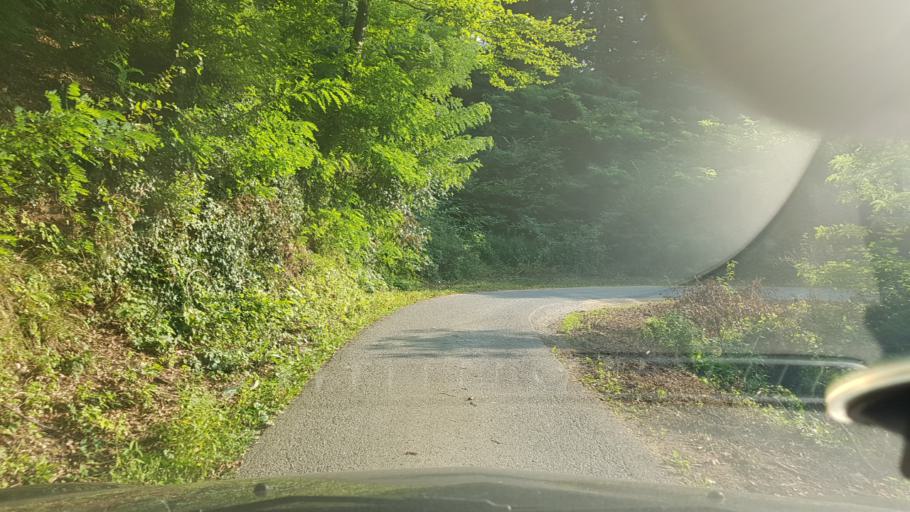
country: HR
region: Krapinsko-Zagorska
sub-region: Grad Krapina
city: Krapina
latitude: 46.1779
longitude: 15.8751
